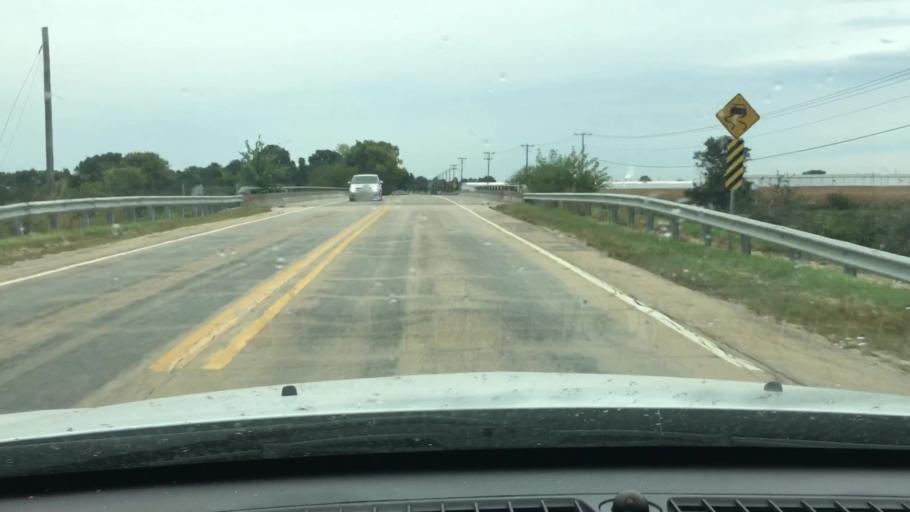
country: US
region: Illinois
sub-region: Ogle County
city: Rochelle
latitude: 41.9001
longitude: -89.0537
